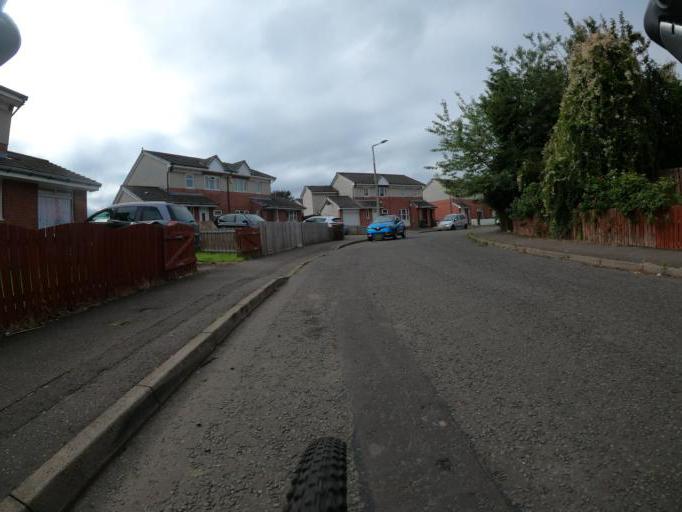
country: GB
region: Scotland
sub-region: Edinburgh
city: Edinburgh
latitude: 55.9742
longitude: -3.2474
